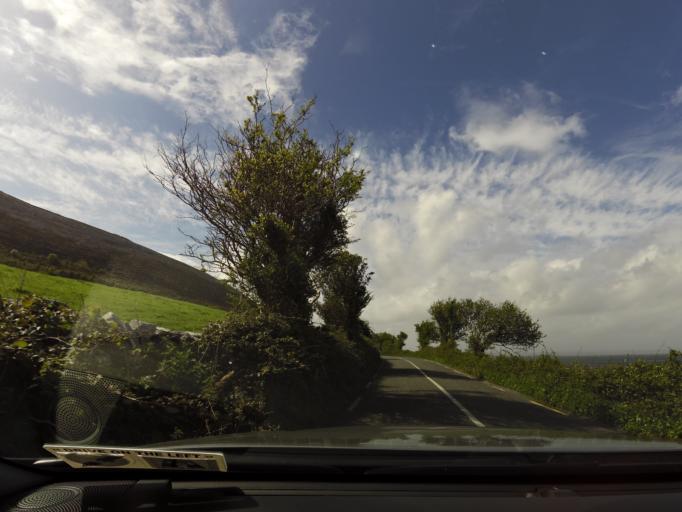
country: IE
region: Connaught
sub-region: County Galway
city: Bearna
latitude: 53.1425
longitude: -9.2308
